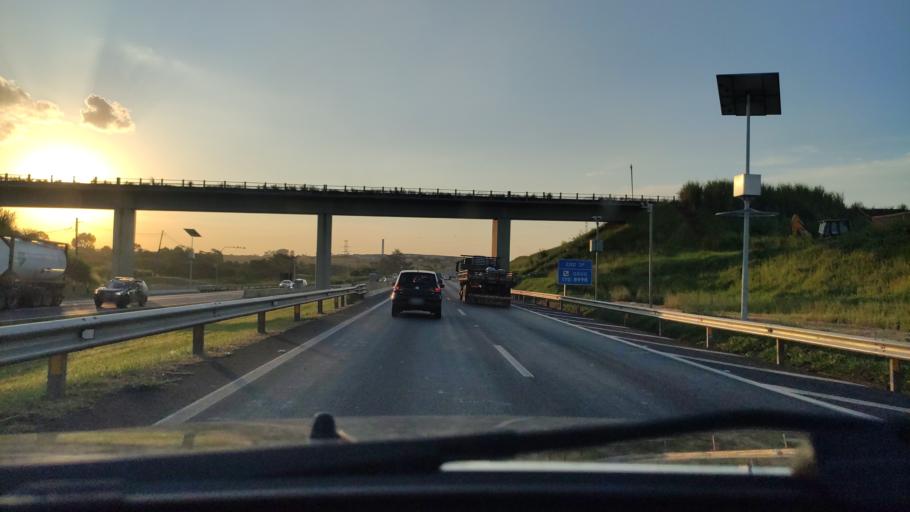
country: BR
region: Sao Paulo
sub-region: Santa Gertrudes
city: Santa Gertrudes
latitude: -22.4545
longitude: -47.5529
